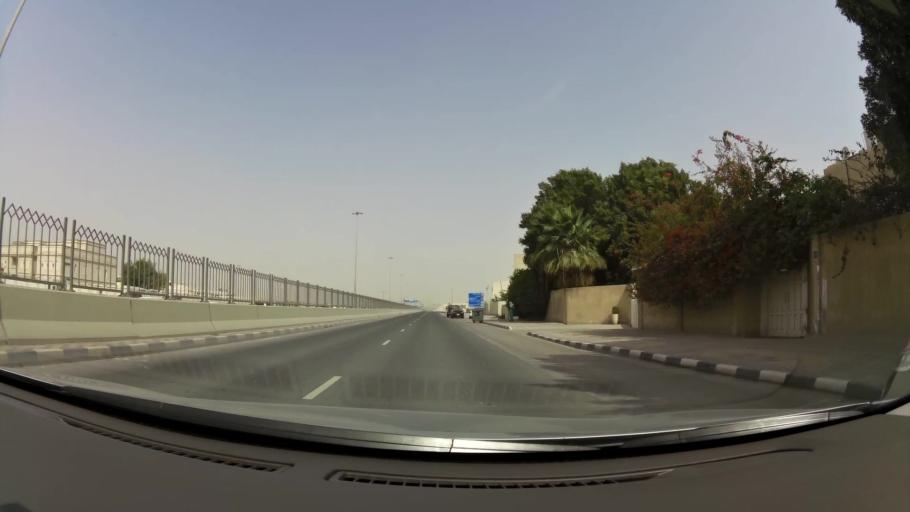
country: QA
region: Baladiyat ad Dawhah
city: Doha
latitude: 25.2796
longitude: 51.4861
